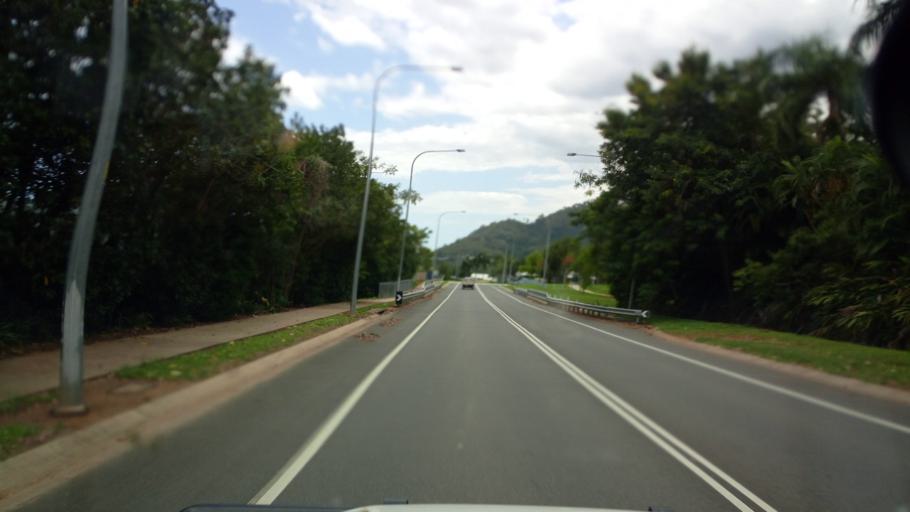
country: AU
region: Queensland
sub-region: Cairns
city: Redlynch
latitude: -16.8969
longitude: 145.6948
